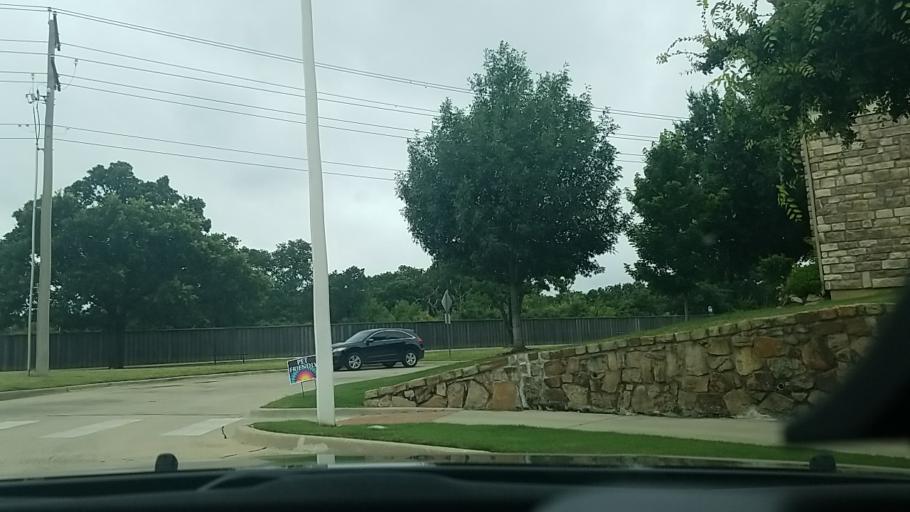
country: US
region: Texas
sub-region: Denton County
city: Corinth
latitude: 33.1836
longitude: -97.0923
